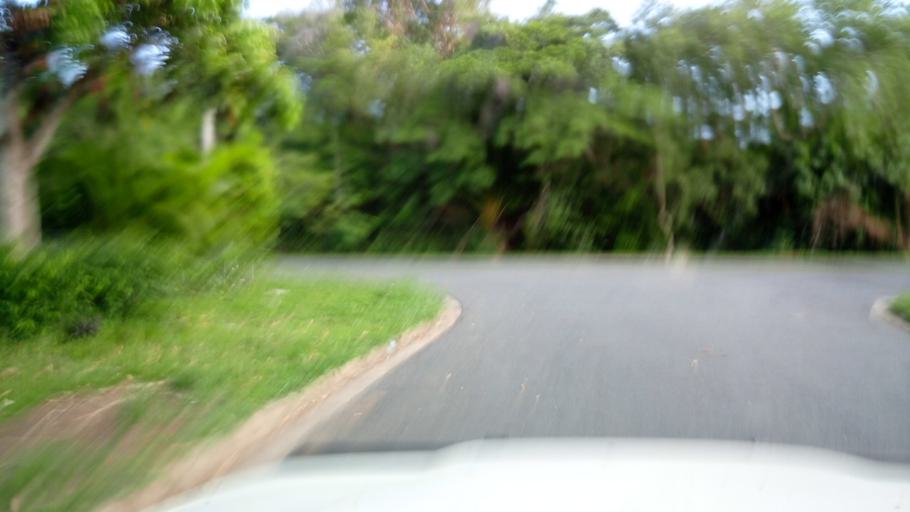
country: AU
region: Queensland
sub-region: Cairns
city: Cairns
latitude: -16.9165
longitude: 145.7565
